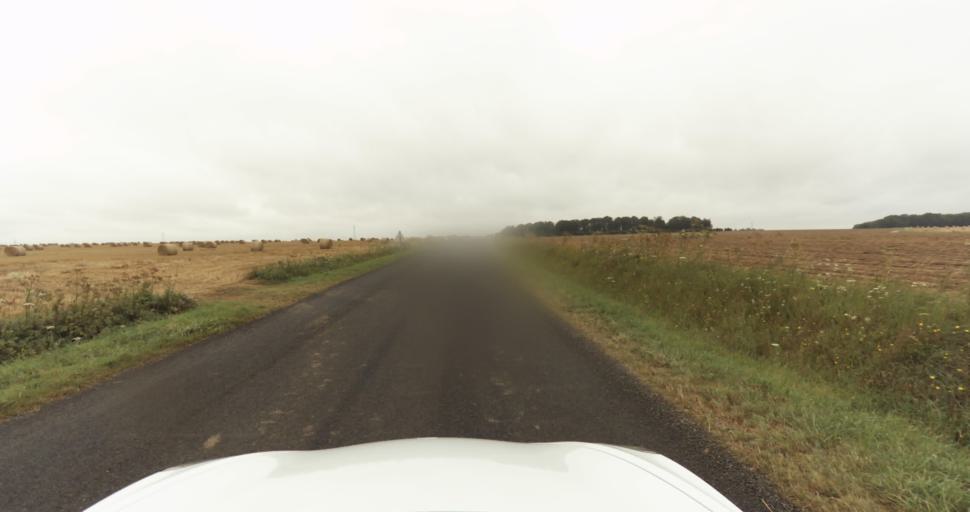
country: FR
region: Haute-Normandie
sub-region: Departement de l'Eure
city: Aviron
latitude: 49.0859
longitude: 1.0696
